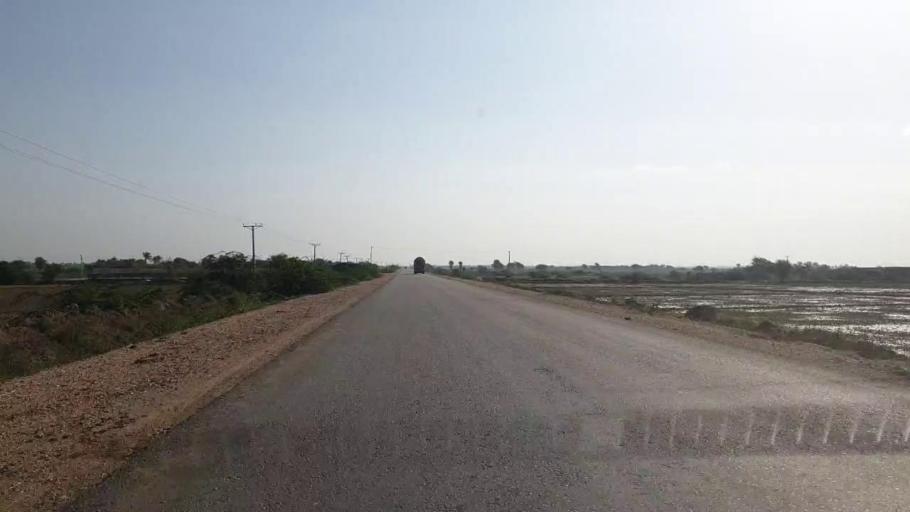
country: PK
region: Sindh
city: Tando Bago
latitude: 24.6575
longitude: 68.9892
